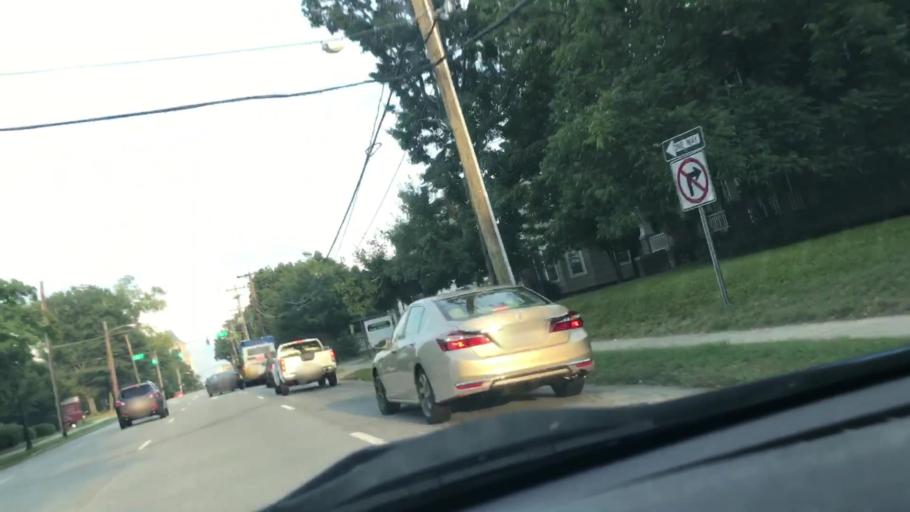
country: US
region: North Carolina
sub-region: Guilford County
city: Greensboro
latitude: 36.0734
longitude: -79.8073
